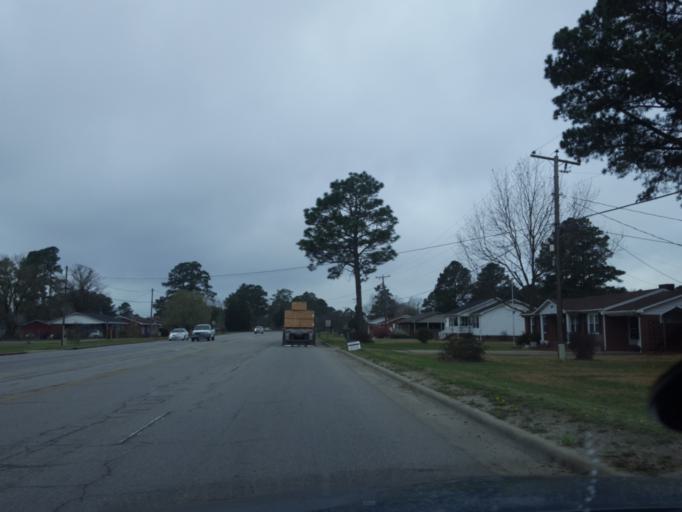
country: US
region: North Carolina
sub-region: Washington County
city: Plymouth
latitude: 35.8322
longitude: -76.7748
